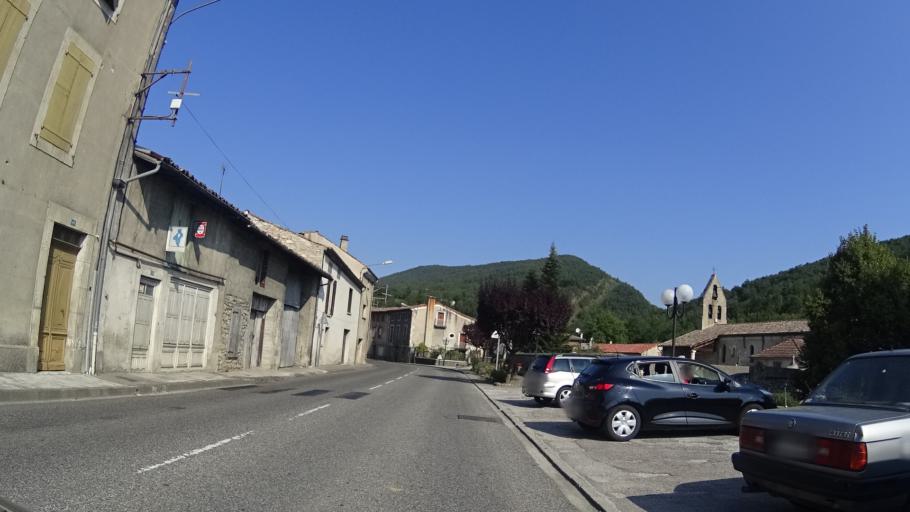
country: FR
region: Midi-Pyrenees
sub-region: Departement de l'Ariege
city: Belesta
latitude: 42.9167
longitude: 1.9026
